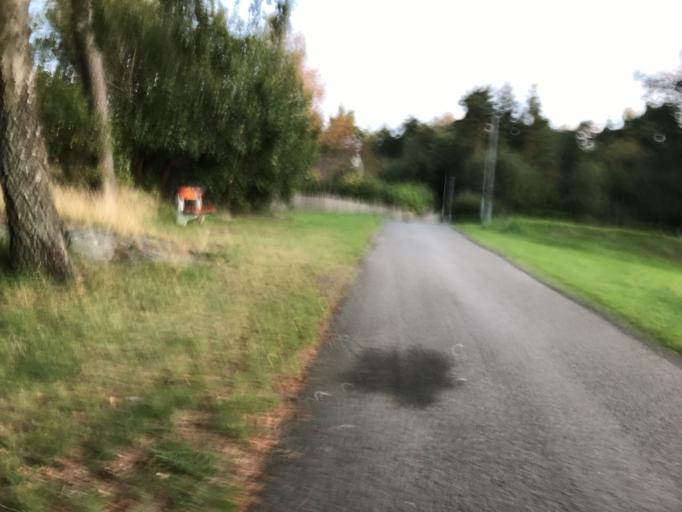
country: SE
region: Vaestra Goetaland
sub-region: Goteborg
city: Majorna
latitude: 57.7224
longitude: 11.8865
